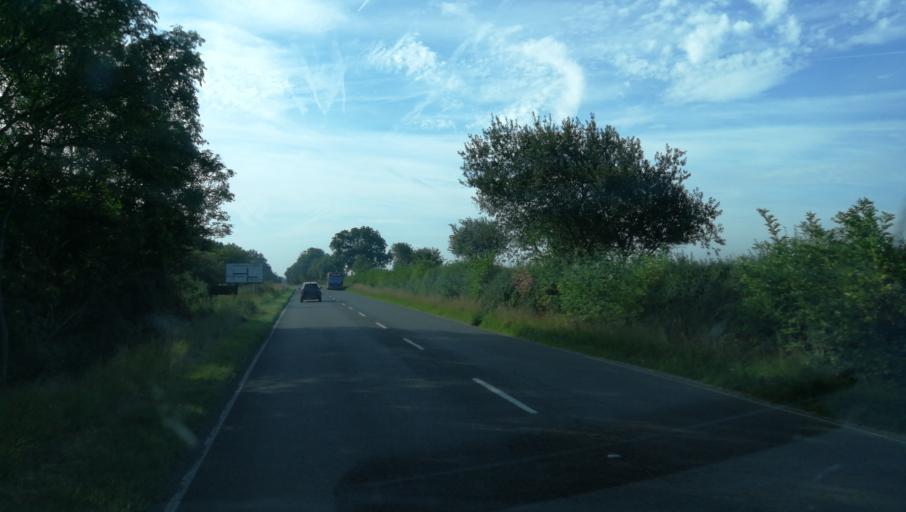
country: GB
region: England
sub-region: Oxfordshire
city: Woodstock
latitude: 51.8648
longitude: -1.3251
